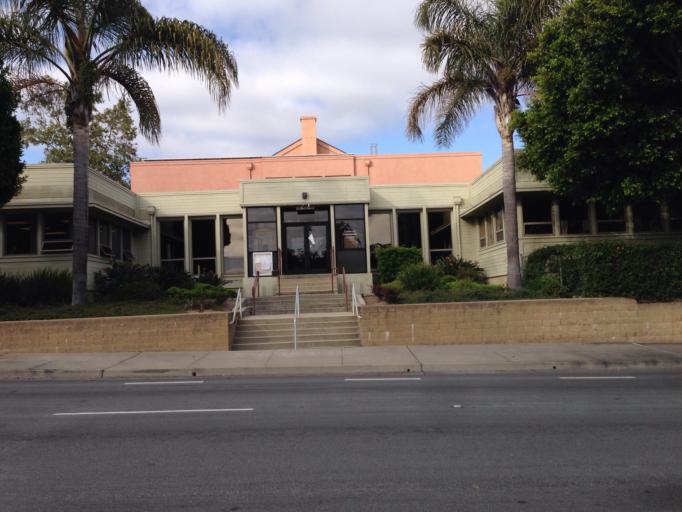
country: US
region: California
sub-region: San Luis Obispo County
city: San Luis Obispo
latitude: 35.2841
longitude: -120.6611
